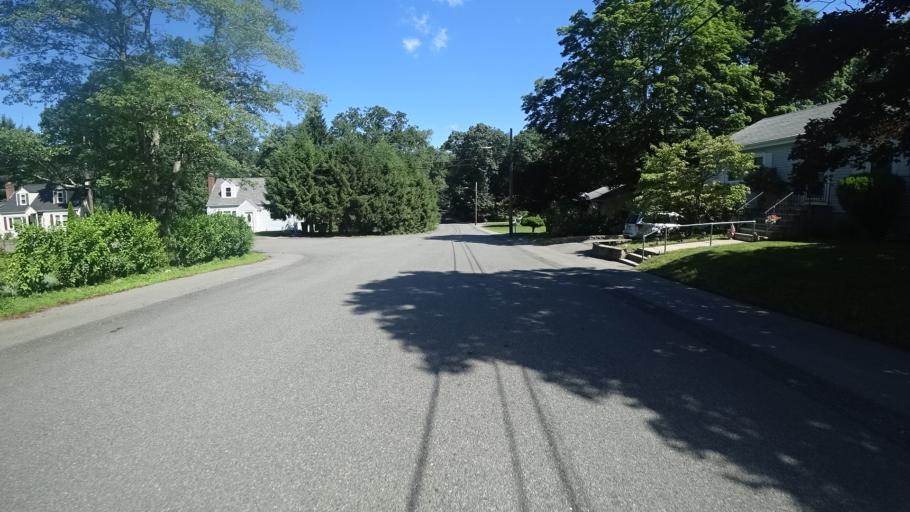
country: US
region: Massachusetts
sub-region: Norfolk County
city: Dedham
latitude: 42.2510
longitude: -71.1461
